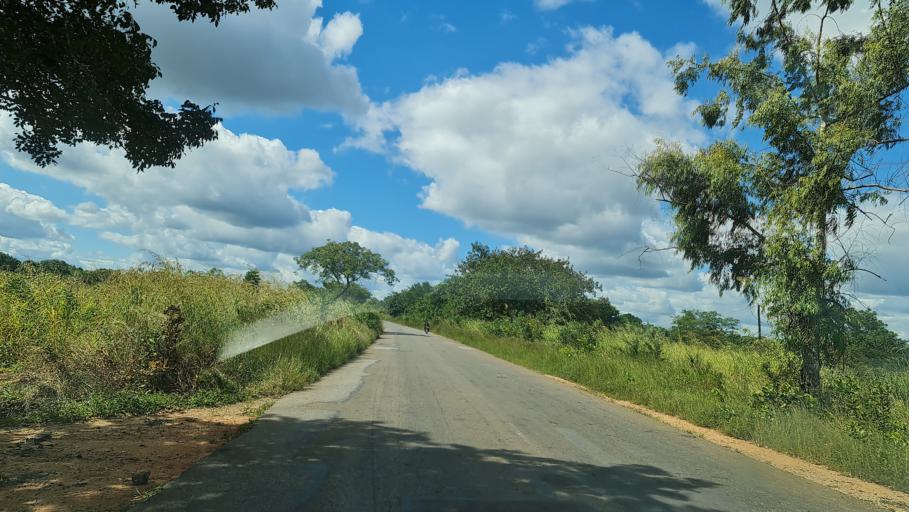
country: MZ
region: Zambezia
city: Quelimane
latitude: -17.5090
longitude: 36.2348
